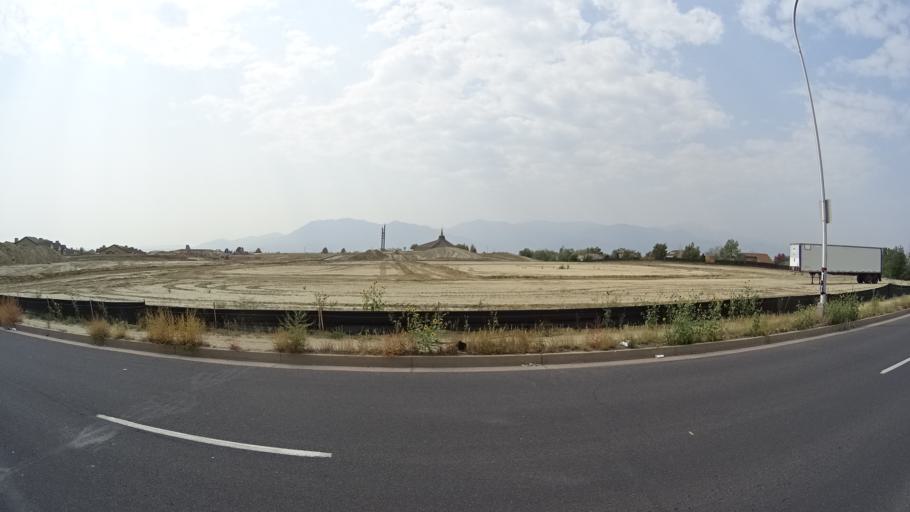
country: US
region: Colorado
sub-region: El Paso County
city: Stratmoor
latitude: 38.8196
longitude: -104.7476
